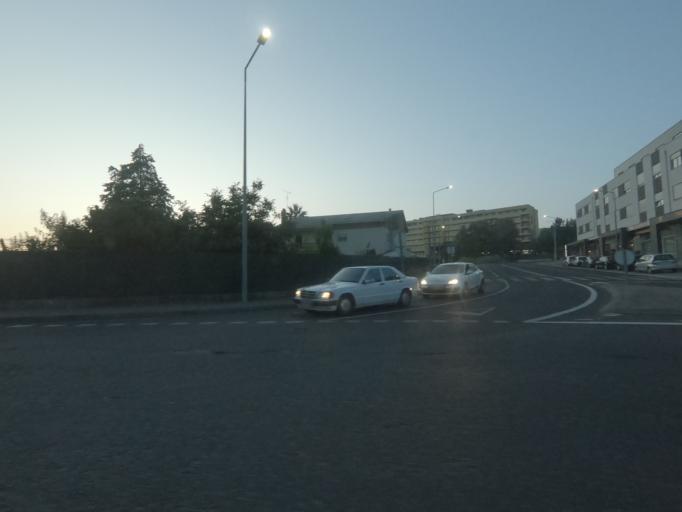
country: PT
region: Leiria
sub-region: Leiria
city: Leiria
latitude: 39.7415
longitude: -8.7933
